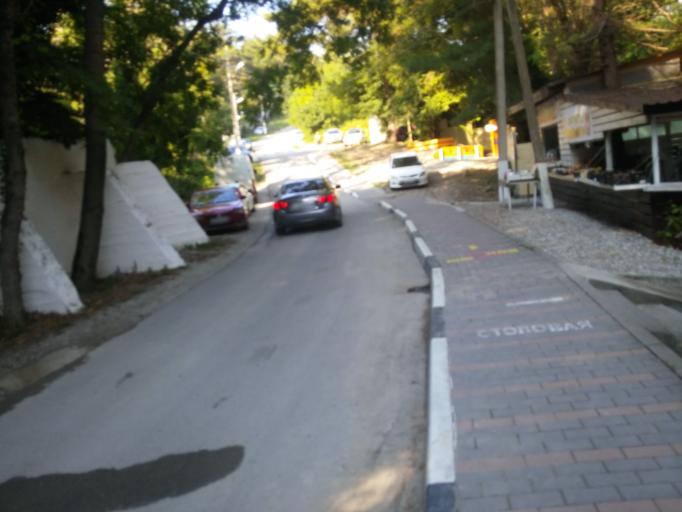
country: RU
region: Krasnodarskiy
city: Divnomorskoye
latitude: 44.4644
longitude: 38.1554
